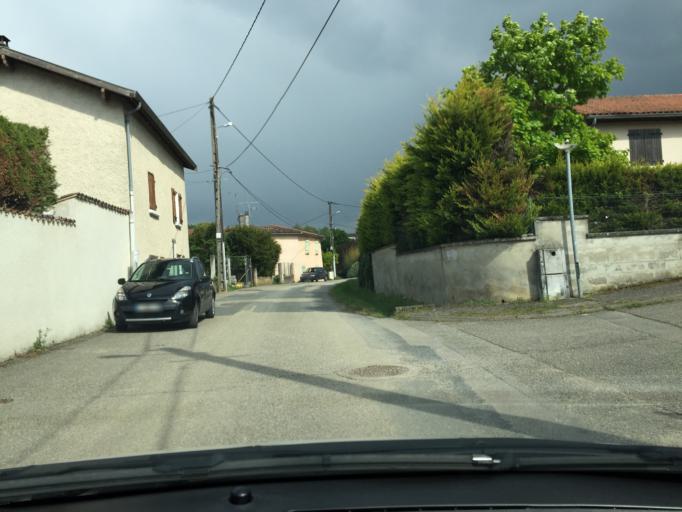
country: FR
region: Rhone-Alpes
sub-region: Departement du Rhone
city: Orlienas
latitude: 45.6597
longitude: 4.7161
